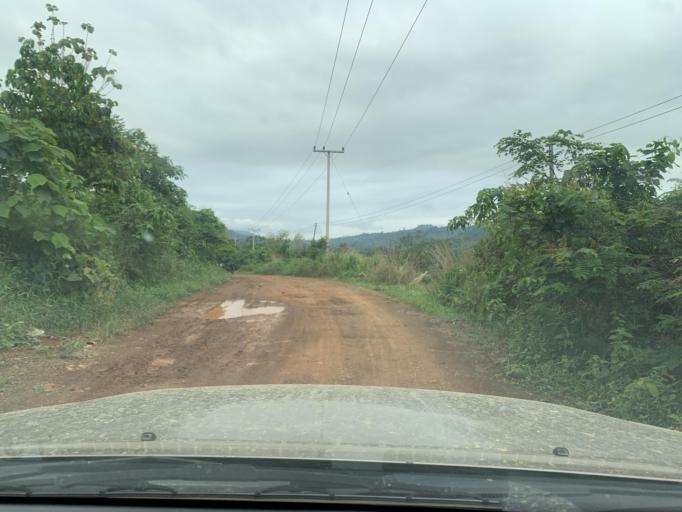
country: TH
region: Nan
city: Mae Charim
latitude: 18.4143
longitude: 101.4428
